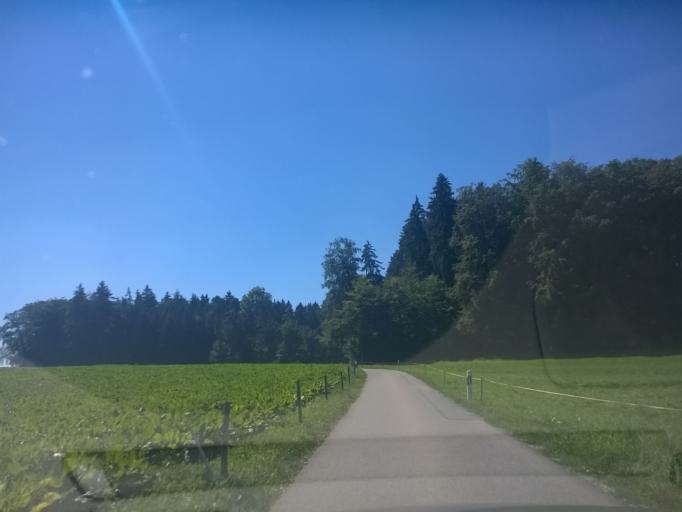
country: CH
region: Zurich
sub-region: Bezirk Winterthur
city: Pfungen
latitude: 47.4980
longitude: 8.6254
